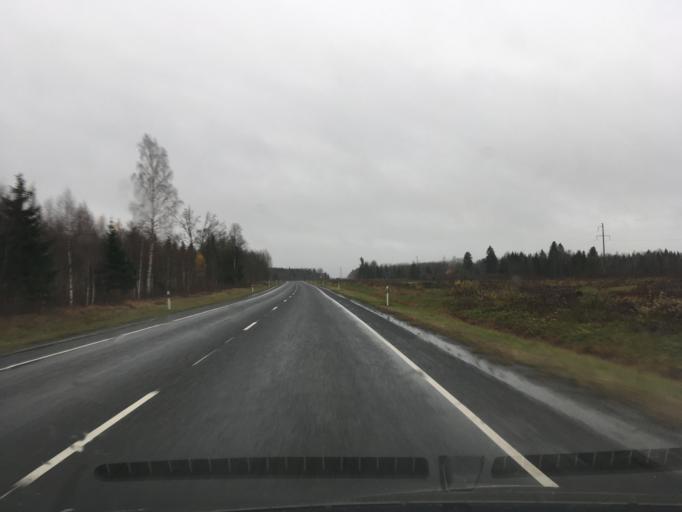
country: EE
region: Harju
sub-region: Nissi vald
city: Turba
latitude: 58.9432
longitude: 24.0867
